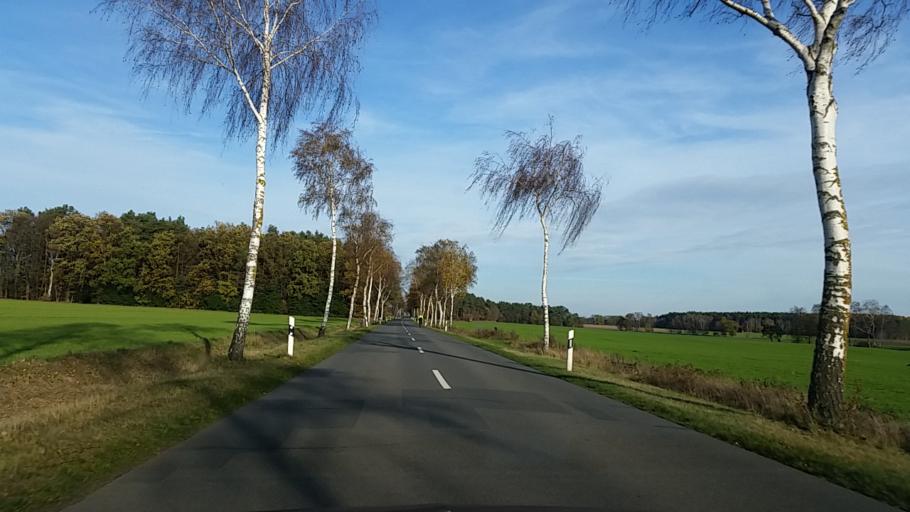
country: DE
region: Lower Saxony
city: Gross Oesingen
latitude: 52.6631
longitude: 10.5036
